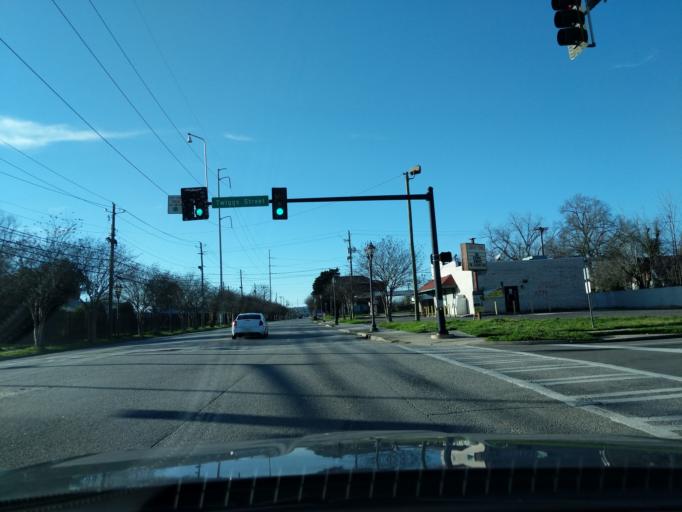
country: US
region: Georgia
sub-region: Richmond County
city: Augusta
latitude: 33.4621
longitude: -81.9693
